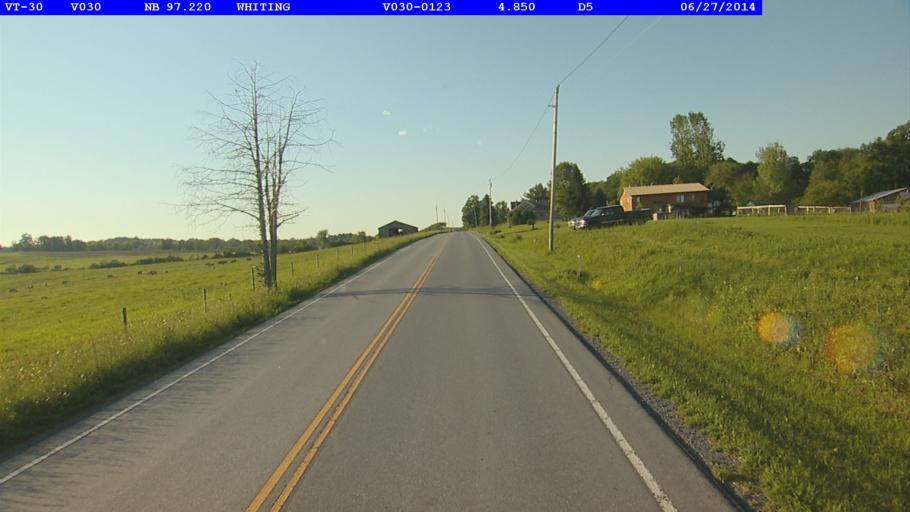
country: US
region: Vermont
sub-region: Addison County
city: Middlebury (village)
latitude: 43.9065
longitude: -73.2083
